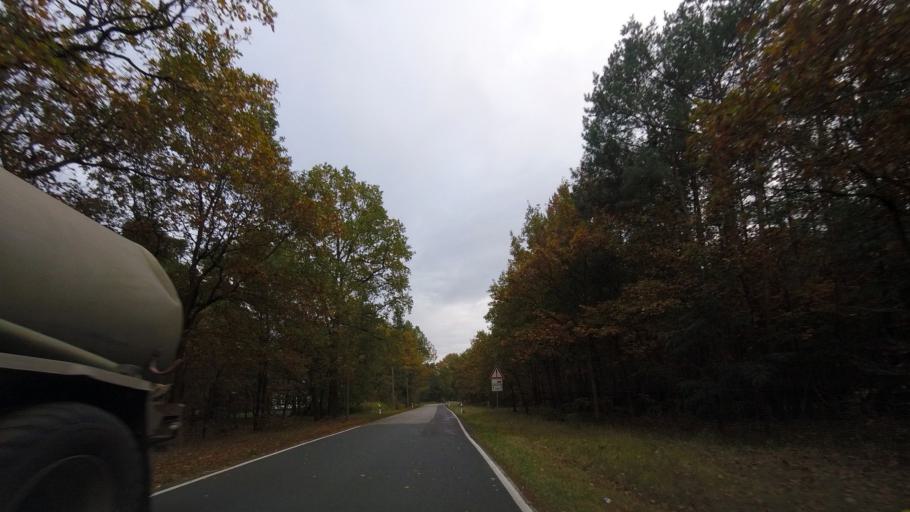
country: DE
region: Brandenburg
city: Treuenbrietzen
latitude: 52.1121
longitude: 12.8798
